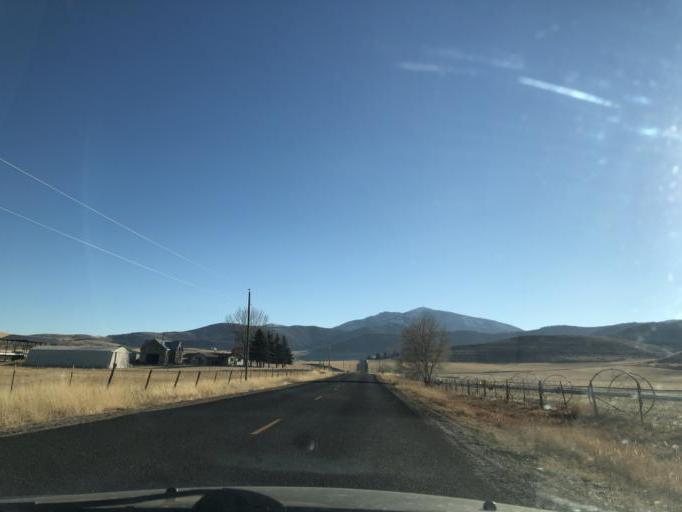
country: US
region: Utah
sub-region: Cache County
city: Wellsville
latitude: 41.6043
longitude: -111.9298
